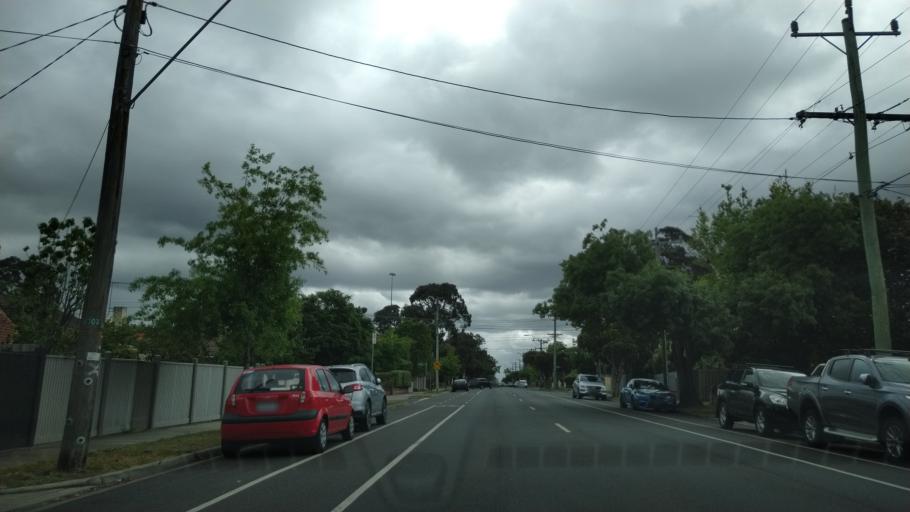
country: AU
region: Victoria
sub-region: Glen Eira
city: Caulfield South
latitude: -37.8968
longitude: 145.0270
